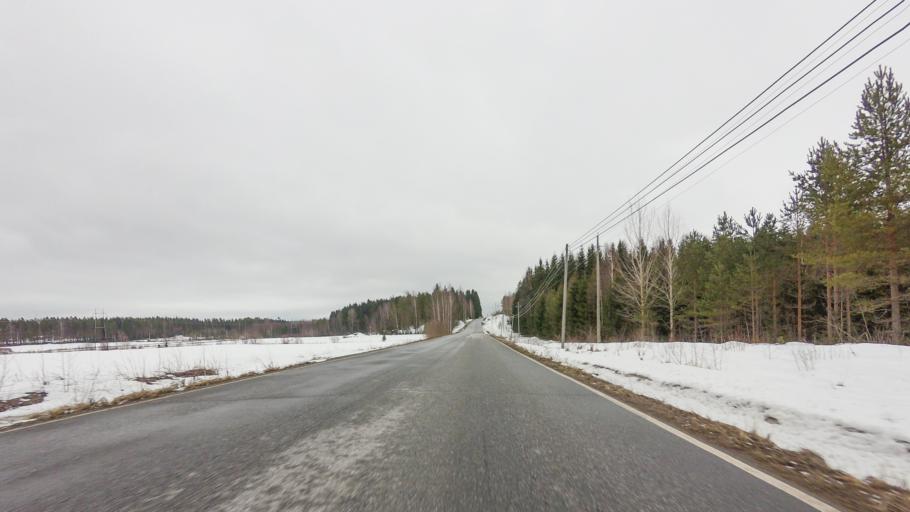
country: FI
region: Southern Savonia
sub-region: Savonlinna
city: Savonlinna
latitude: 61.9511
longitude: 28.8583
